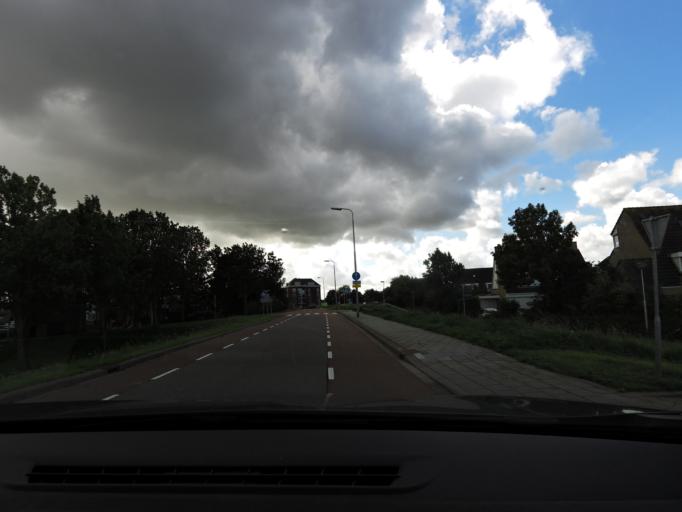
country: NL
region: South Holland
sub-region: Gemeente Oud-Beijerland
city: Oud-Beijerland
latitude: 51.8281
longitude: 4.4083
